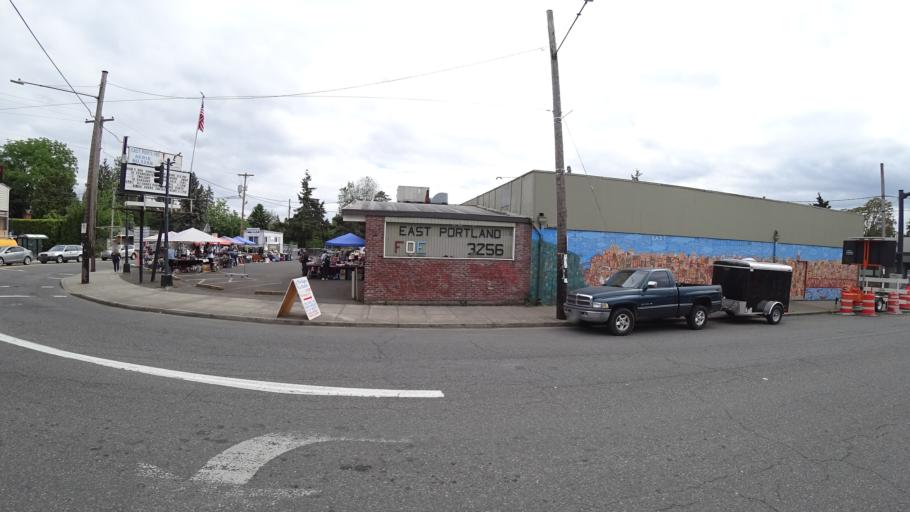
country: US
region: Oregon
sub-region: Multnomah County
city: Lents
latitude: 45.5120
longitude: -122.6119
